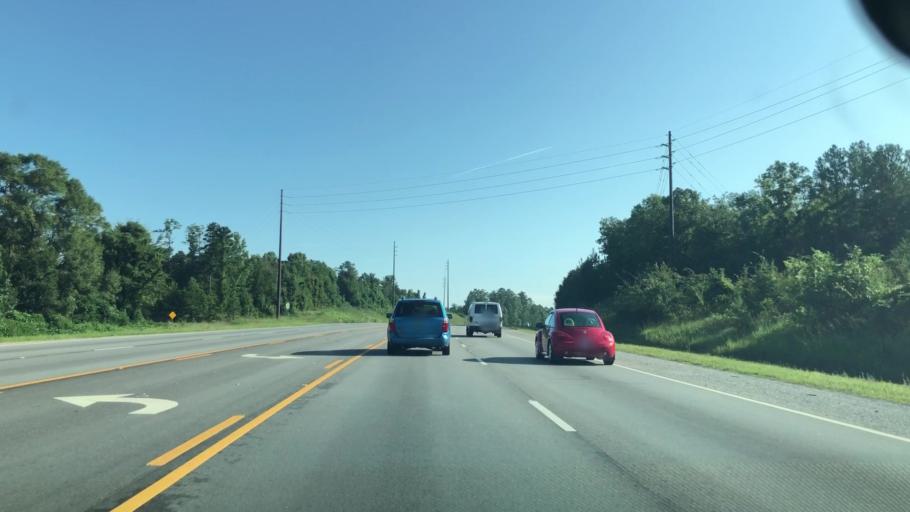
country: US
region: Alabama
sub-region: Calhoun County
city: Bynum
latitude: 33.6124
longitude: -85.9285
